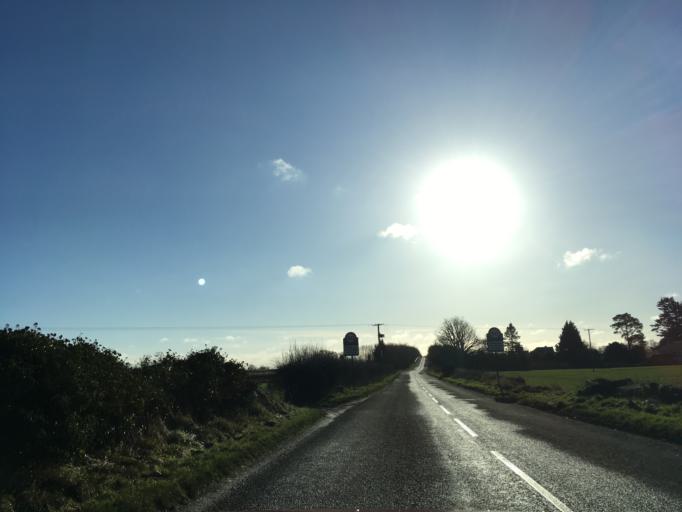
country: GB
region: England
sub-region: Wiltshire
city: Nettleton
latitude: 51.5241
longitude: -2.2763
